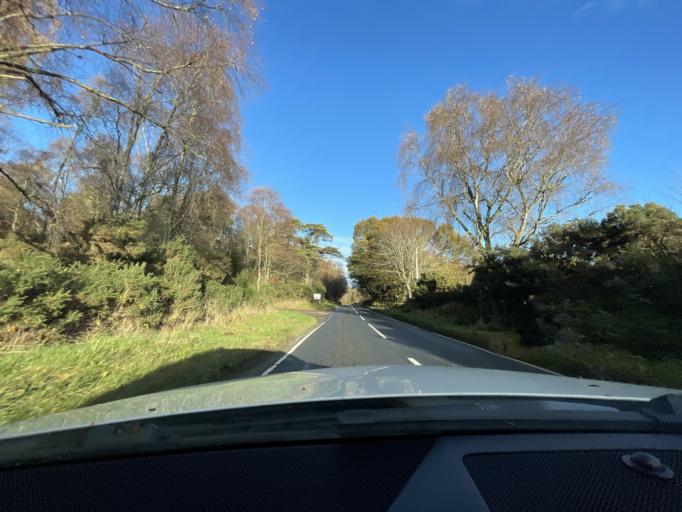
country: GB
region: Scotland
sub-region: Highland
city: Inverness
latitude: 57.4199
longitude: -4.2979
